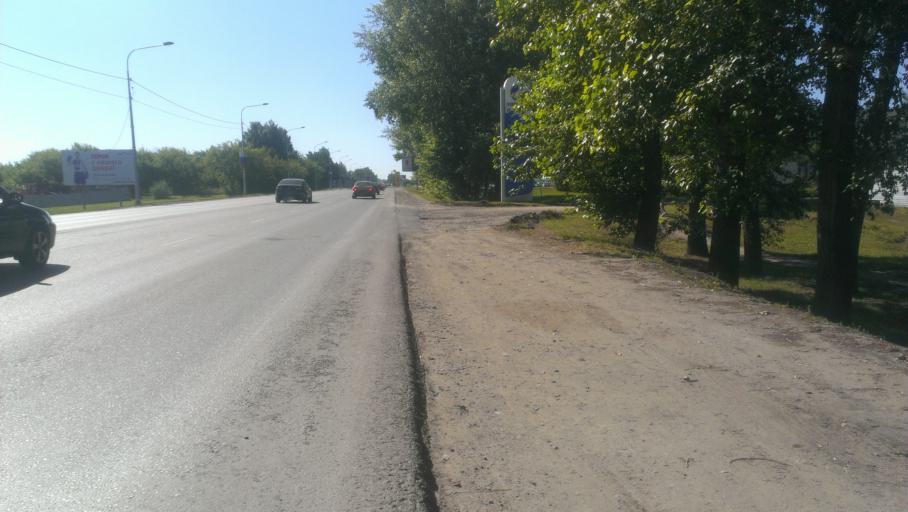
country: RU
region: Altai Krai
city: Novosilikatnyy
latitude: 53.3473
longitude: 83.6426
